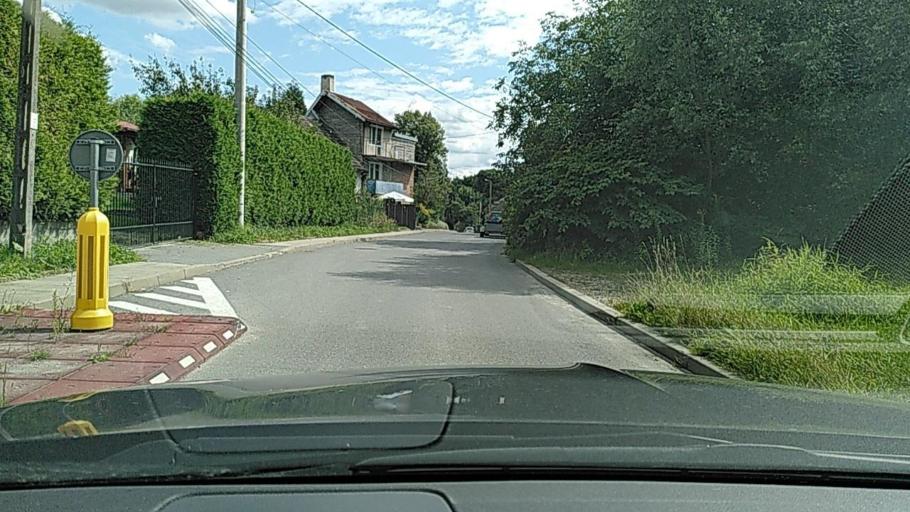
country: PL
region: Lesser Poland Voivodeship
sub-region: Powiat krakowski
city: Rzaska
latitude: 50.0893
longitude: 19.8725
